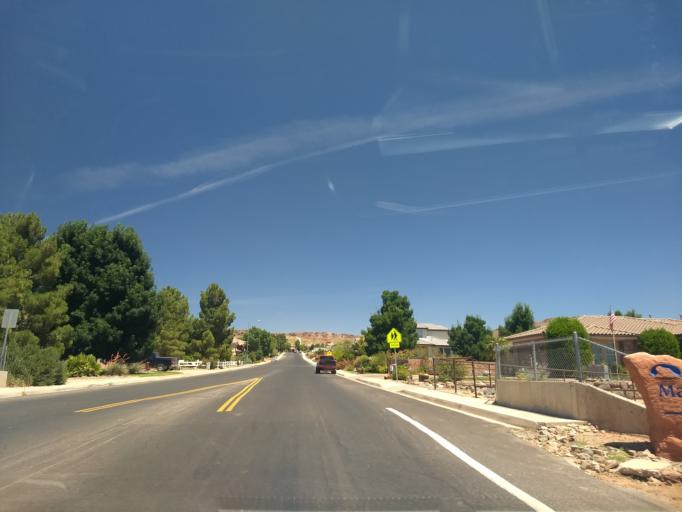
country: US
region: Utah
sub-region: Washington County
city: Washington
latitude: 37.0889
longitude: -113.4968
